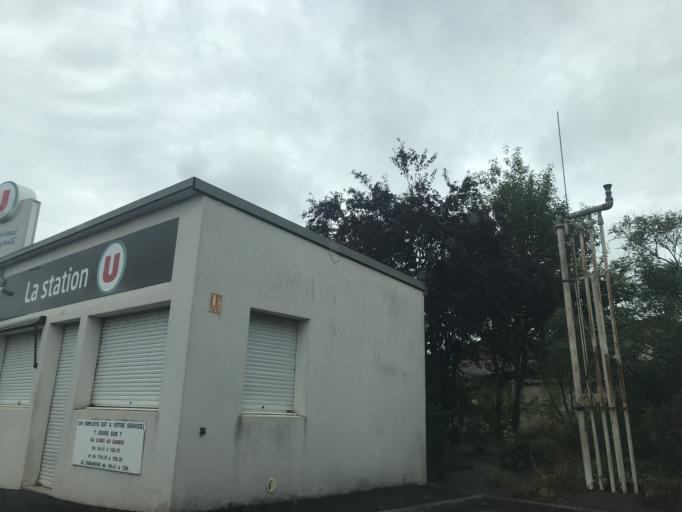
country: FR
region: Auvergne
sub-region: Departement du Puy-de-Dome
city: Arlanc
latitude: 45.4184
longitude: 3.7278
